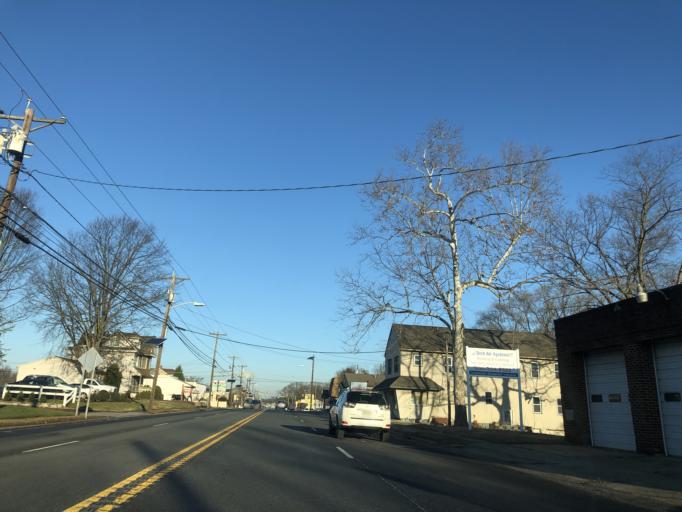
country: US
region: New Jersey
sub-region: Camden County
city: Somerdale
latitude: 39.8460
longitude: -75.0201
